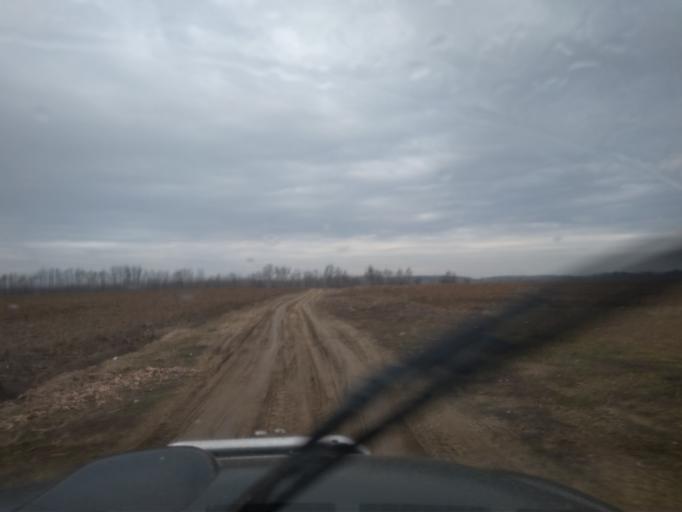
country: HU
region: Szabolcs-Szatmar-Bereg
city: Apagy
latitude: 47.9684
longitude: 21.9224
